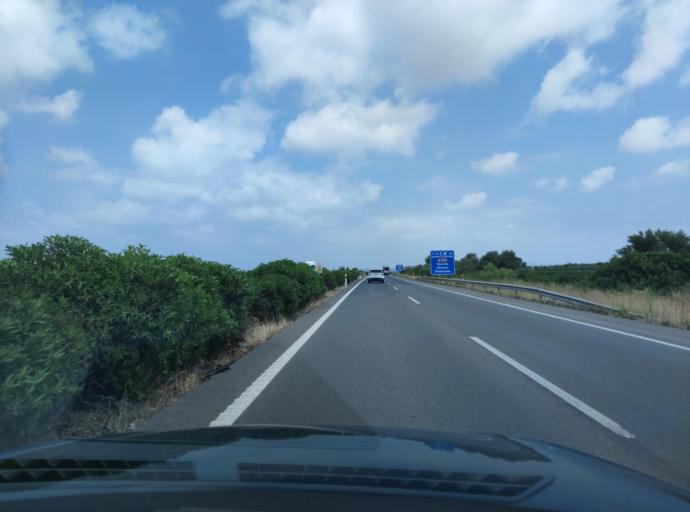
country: ES
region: Valencia
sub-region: Provincia de Castello
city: Vinaros
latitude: 40.5095
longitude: 0.4155
